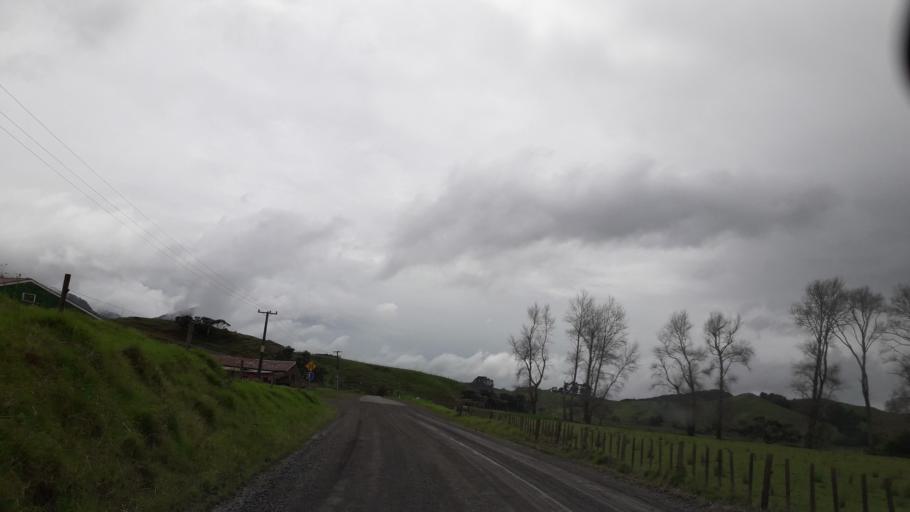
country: NZ
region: Northland
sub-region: Far North District
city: Ahipara
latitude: -35.4261
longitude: 173.3567
